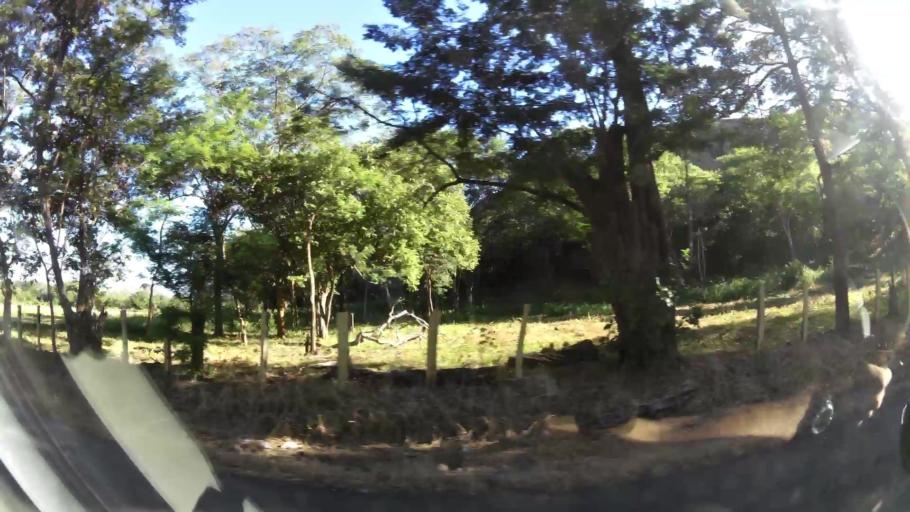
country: CR
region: Guanacaste
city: Sardinal
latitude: 10.5019
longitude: -85.6448
